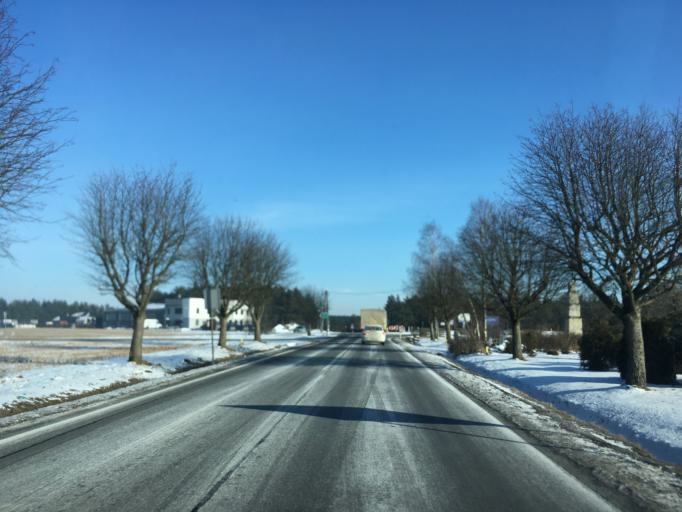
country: PL
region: Pomeranian Voivodeship
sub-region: Powiat koscierski
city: Lipusz
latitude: 54.1304
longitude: 17.8614
